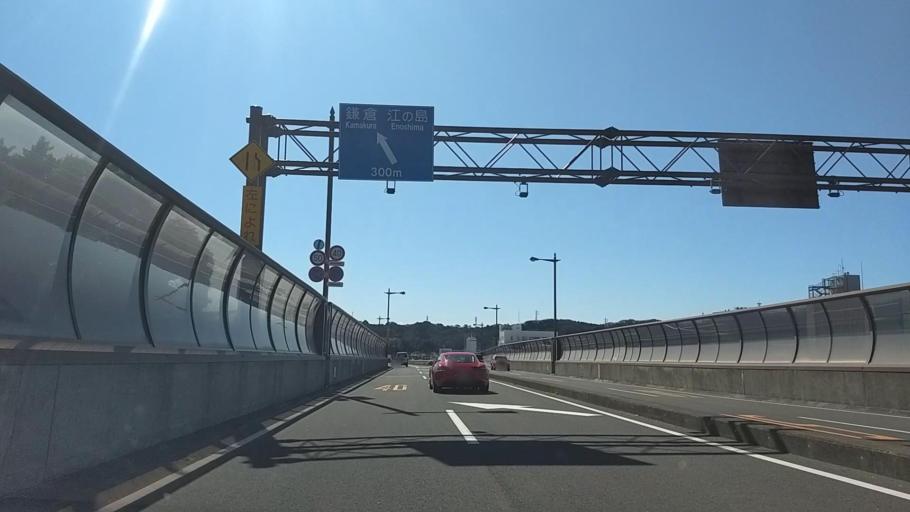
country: JP
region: Kanagawa
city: Fujisawa
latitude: 35.3372
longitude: 139.5021
